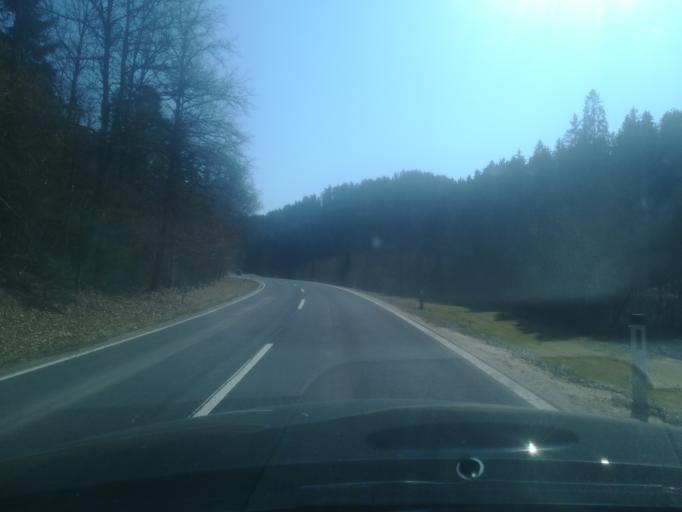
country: AT
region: Upper Austria
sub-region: Politischer Bezirk Freistadt
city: Freistadt
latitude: 48.4422
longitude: 14.5522
